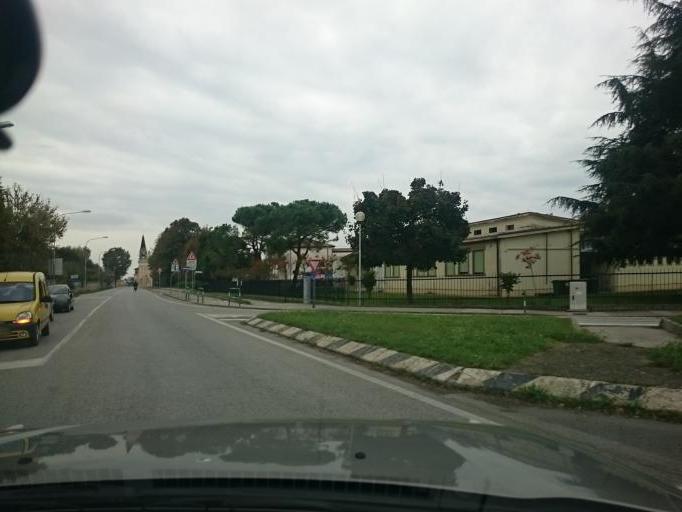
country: IT
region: Veneto
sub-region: Provincia di Padova
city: Arzergrande
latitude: 45.2770
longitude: 12.0289
